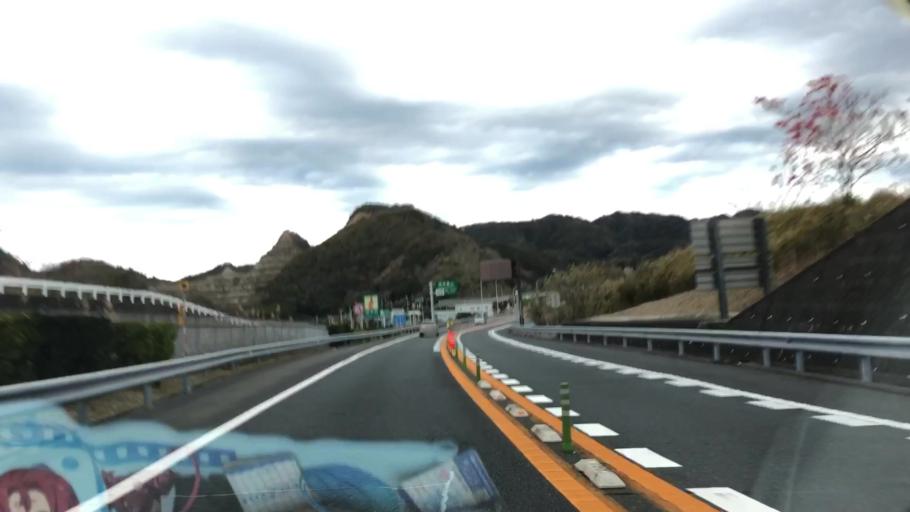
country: JP
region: Chiba
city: Tateyama
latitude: 35.1101
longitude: 139.8506
